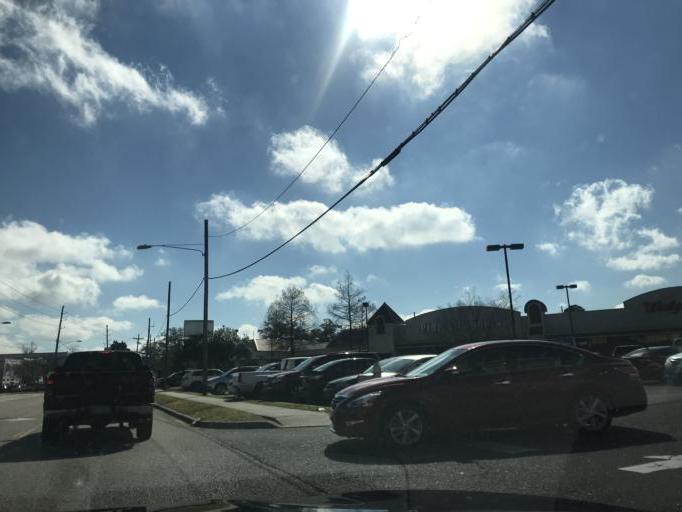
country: US
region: Louisiana
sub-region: Jefferson Parish
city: Metairie
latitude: 29.9883
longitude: -90.1314
